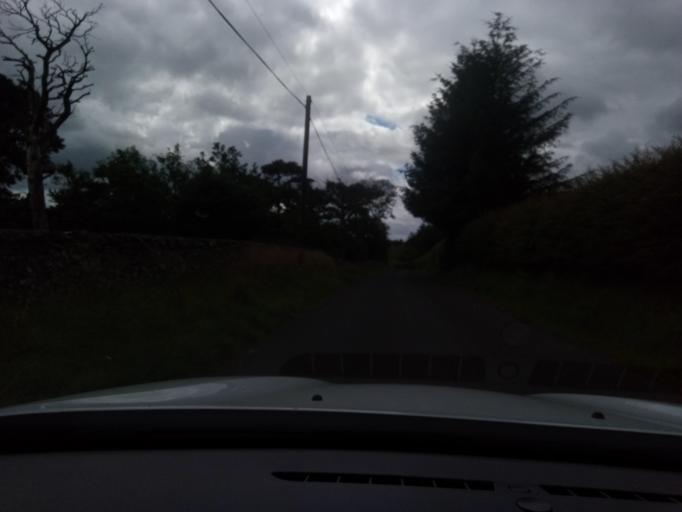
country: GB
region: Scotland
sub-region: The Scottish Borders
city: Innerleithen
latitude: 55.4519
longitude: -3.1021
